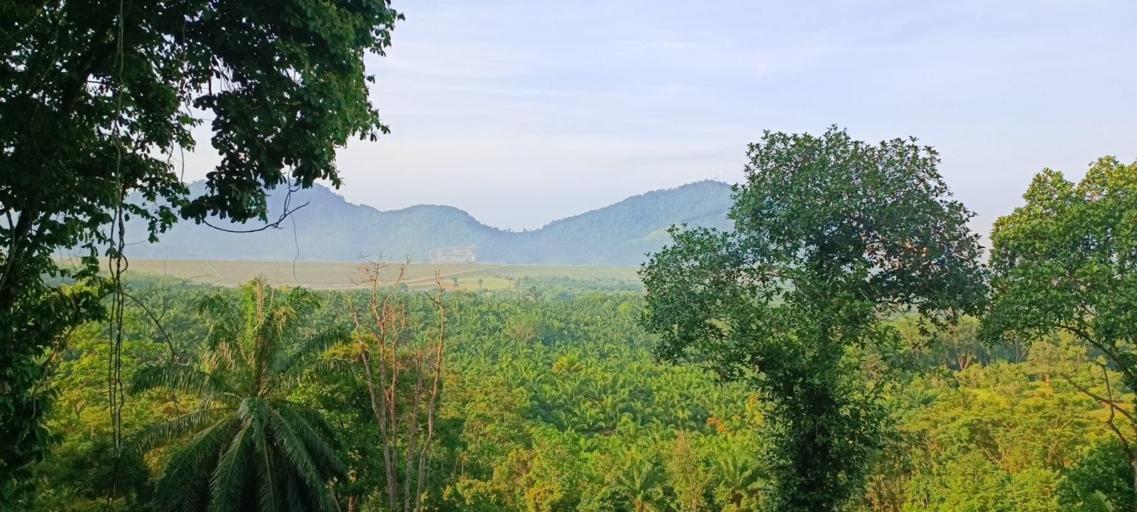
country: MY
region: Penang
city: Bukit Mertajam
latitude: 5.4052
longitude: 100.5053
